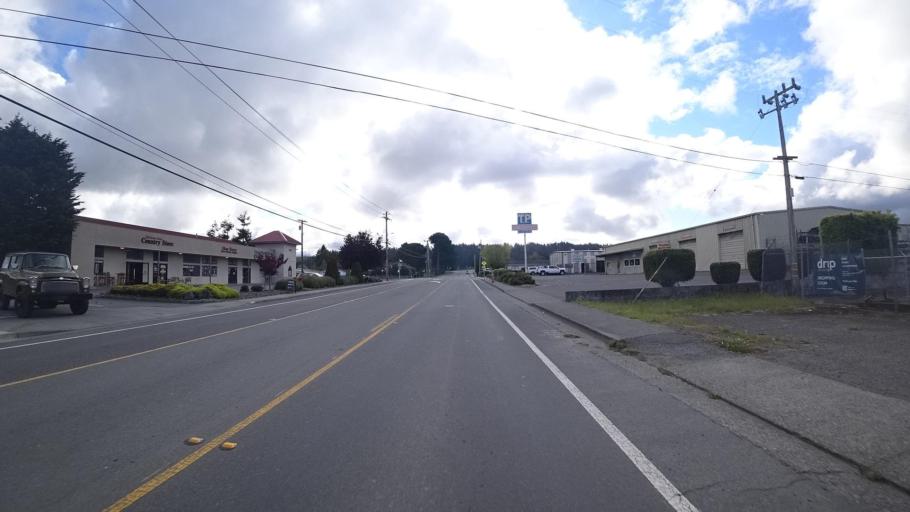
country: US
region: California
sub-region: Humboldt County
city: Arcata
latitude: 40.9049
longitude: -124.0783
